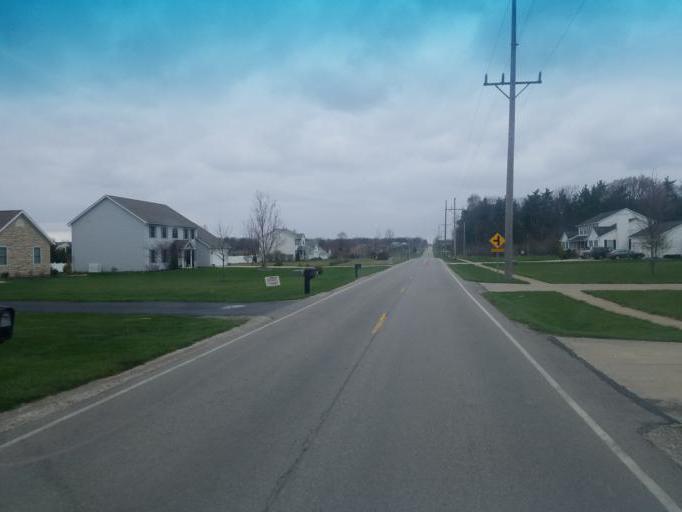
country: US
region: Ohio
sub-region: Marion County
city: Marion
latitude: 40.5237
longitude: -83.1509
